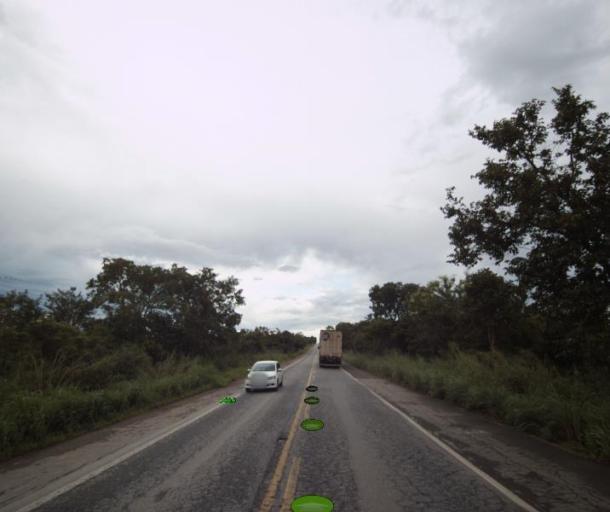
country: BR
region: Goias
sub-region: Porangatu
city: Porangatu
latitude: -13.6518
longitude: -49.0383
